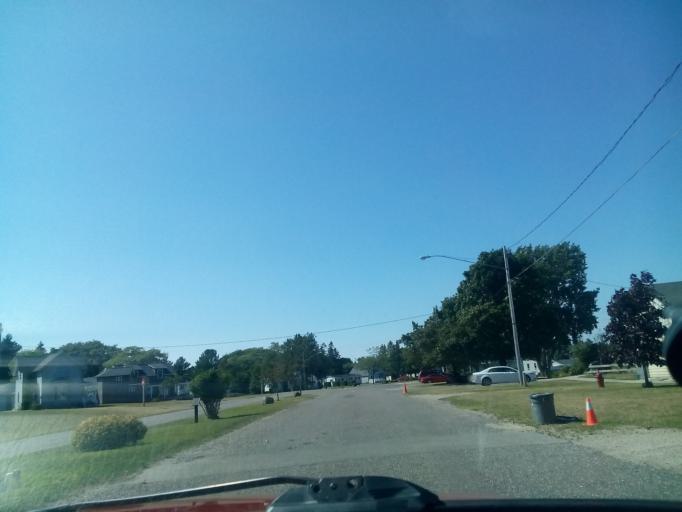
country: US
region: Michigan
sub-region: Mackinac County
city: Saint Ignace
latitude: 45.7841
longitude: -84.7245
